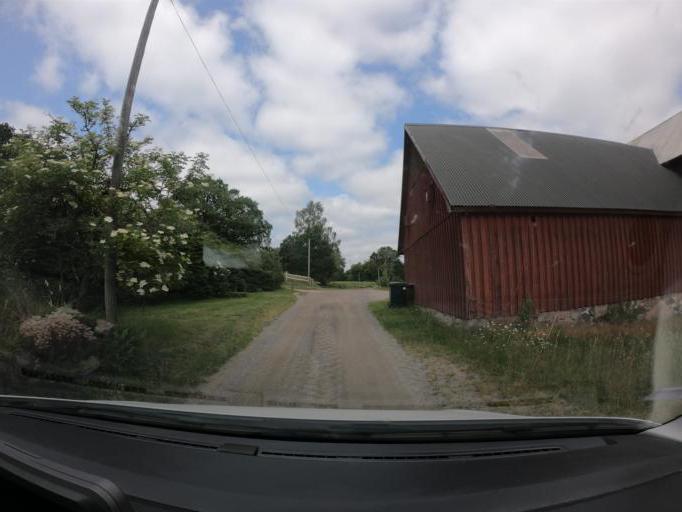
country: SE
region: Skane
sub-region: Hassleholms Kommun
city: Sosdala
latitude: 56.0509
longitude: 13.5712
